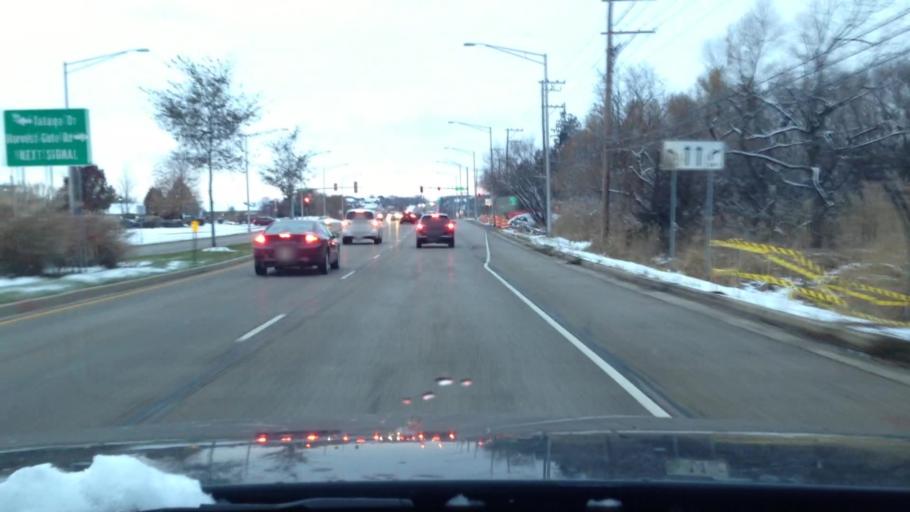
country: US
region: Illinois
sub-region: McHenry County
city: Lake in the Hills
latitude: 42.1758
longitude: -88.3398
